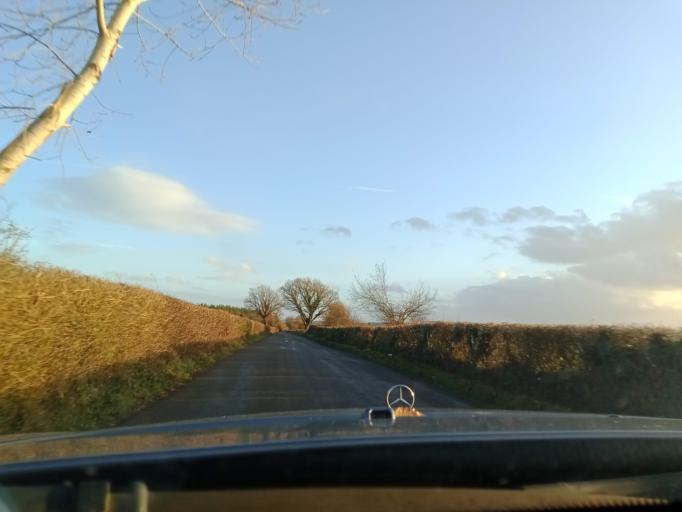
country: IE
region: Leinster
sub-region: Kilkenny
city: Callan
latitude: 52.4963
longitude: -7.3344
